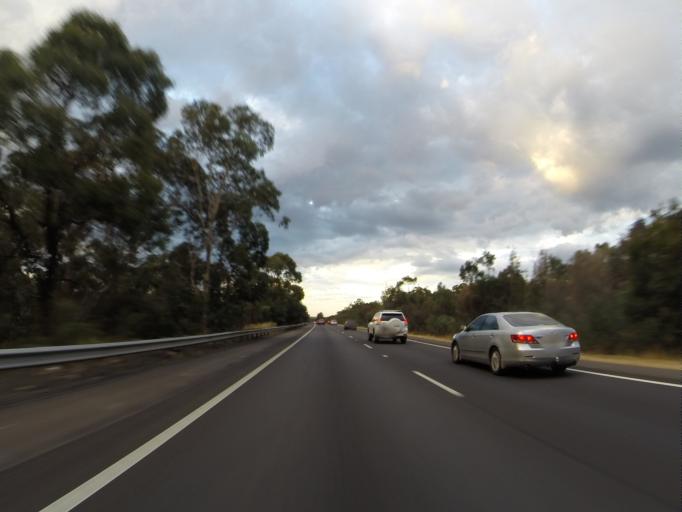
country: AU
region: New South Wales
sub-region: Wollondilly
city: Douglas Park
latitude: -34.2006
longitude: 150.7038
